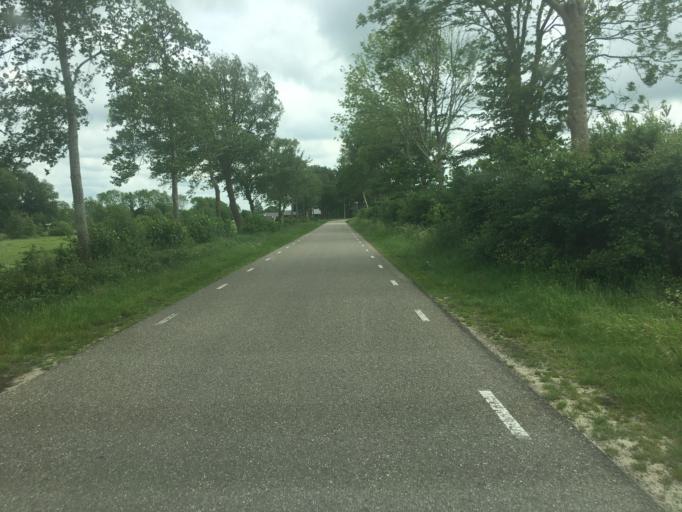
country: NL
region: Friesland
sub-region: Gemeente Heerenveen
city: Heerenveen
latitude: 52.9268
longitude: 5.9232
